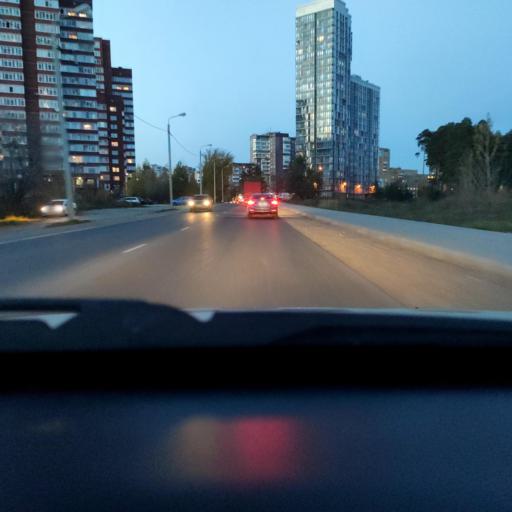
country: RU
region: Perm
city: Kondratovo
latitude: 57.9903
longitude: 56.1358
